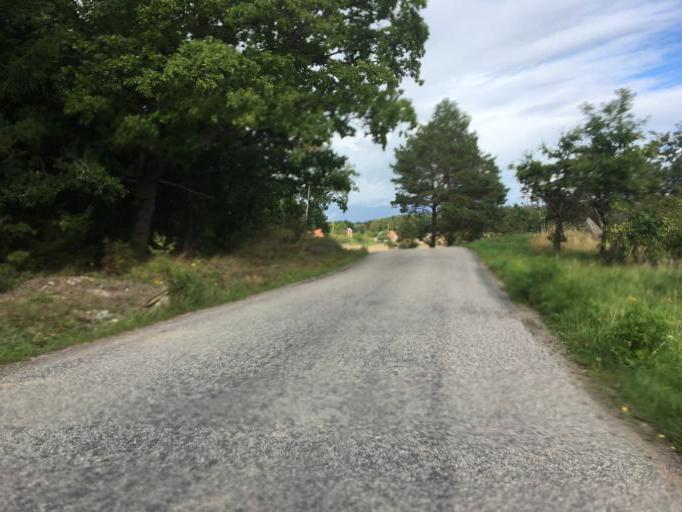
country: SE
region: Soedermanland
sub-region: Eskilstuna Kommun
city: Eskilstuna
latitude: 59.4448
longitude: 16.6406
